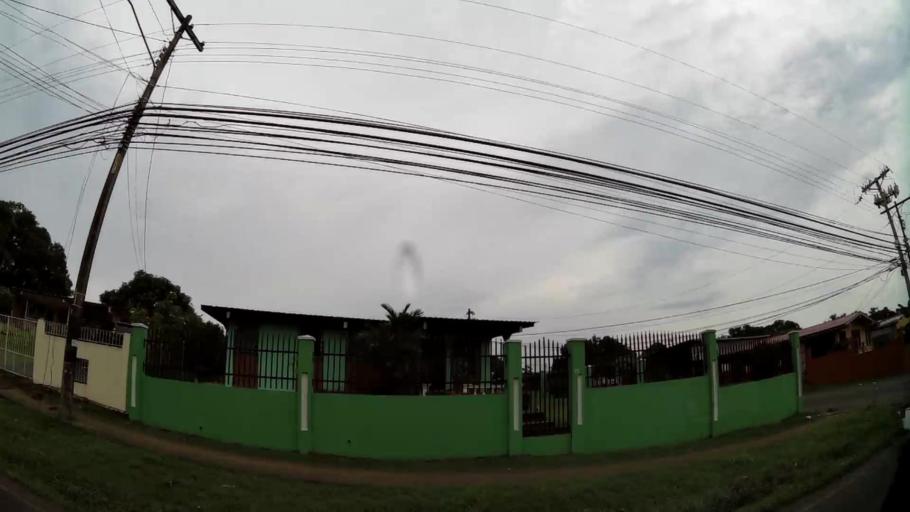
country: PA
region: Panama
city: San Miguelito
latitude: 9.0467
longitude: -79.4390
